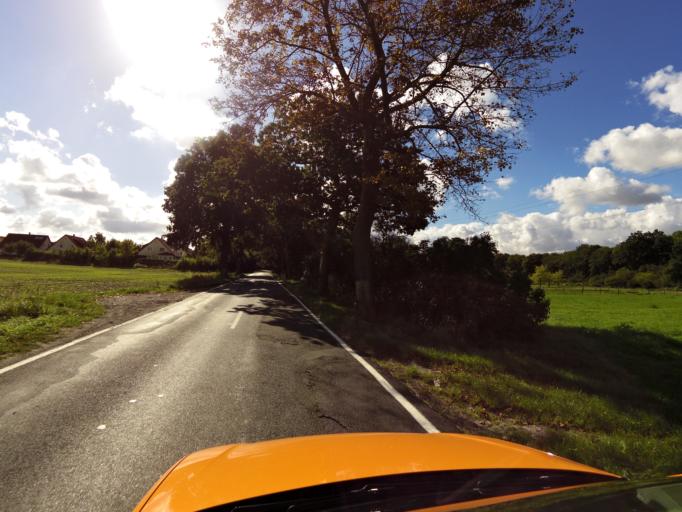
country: DE
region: Brandenburg
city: Michendorf
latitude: 52.2489
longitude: 13.0814
